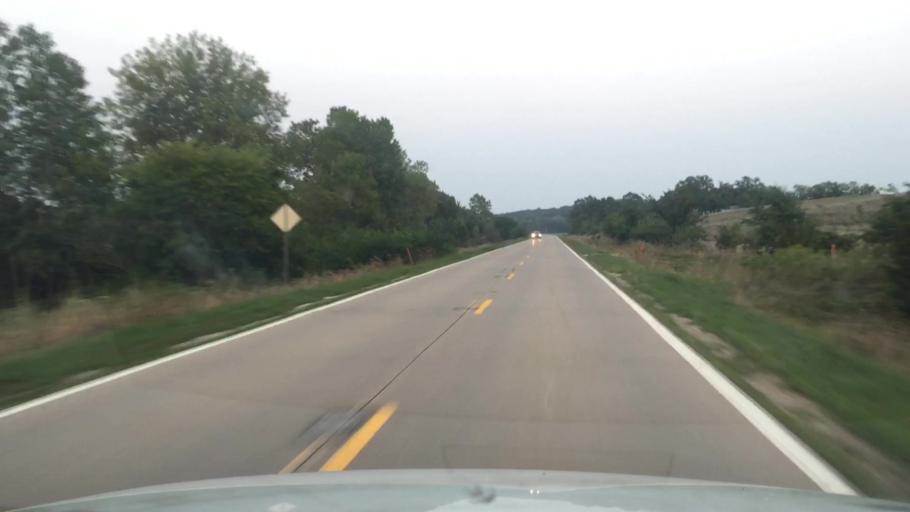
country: US
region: Iowa
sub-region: Warren County
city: Indianola
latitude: 41.1897
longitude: -93.6296
